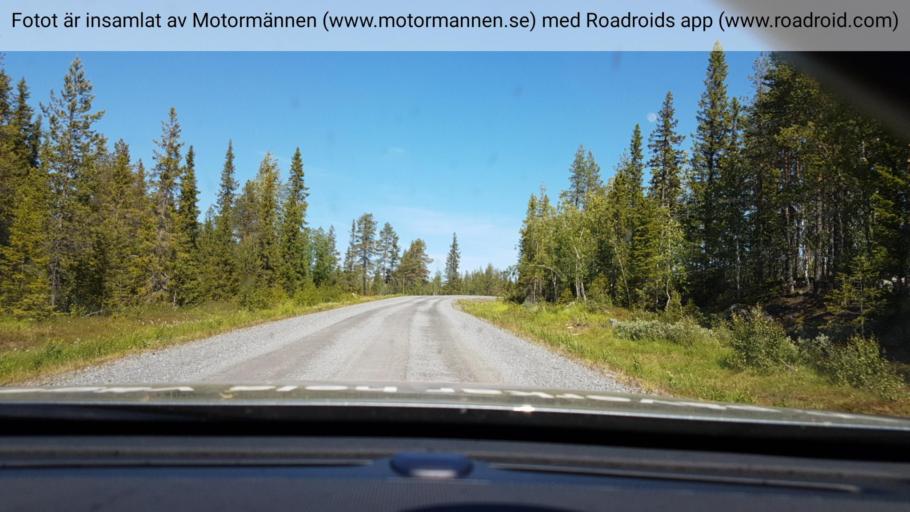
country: SE
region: Vaesterbotten
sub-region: Vilhelmina Kommun
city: Sjoberg
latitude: 64.7001
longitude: 15.7582
